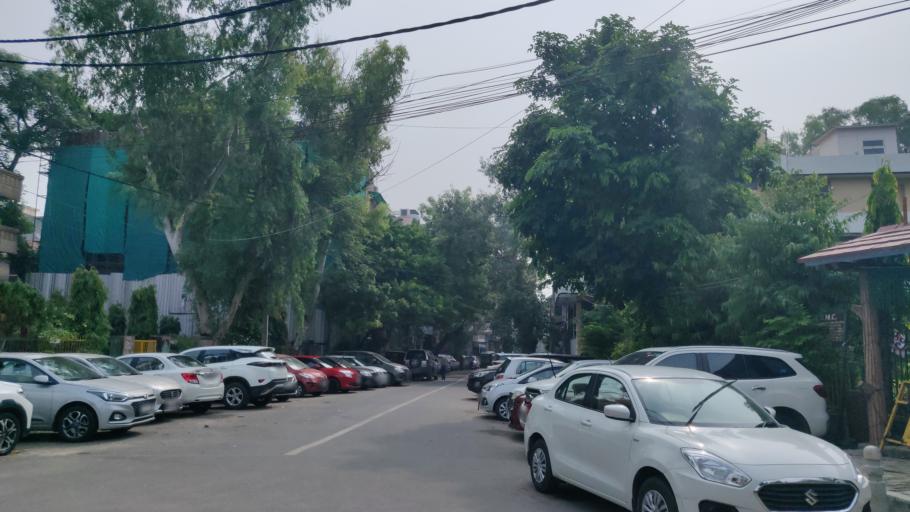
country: IN
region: NCT
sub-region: New Delhi
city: New Delhi
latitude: 28.5721
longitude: 77.2392
